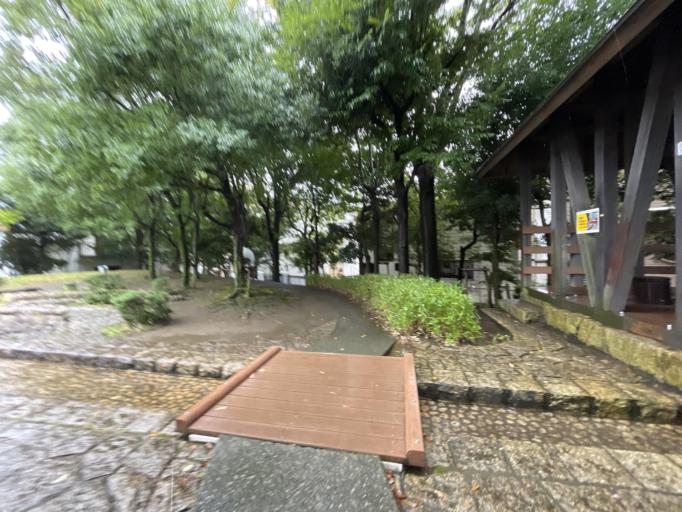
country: JP
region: Kanagawa
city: Zama
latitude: 35.5467
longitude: 139.3293
